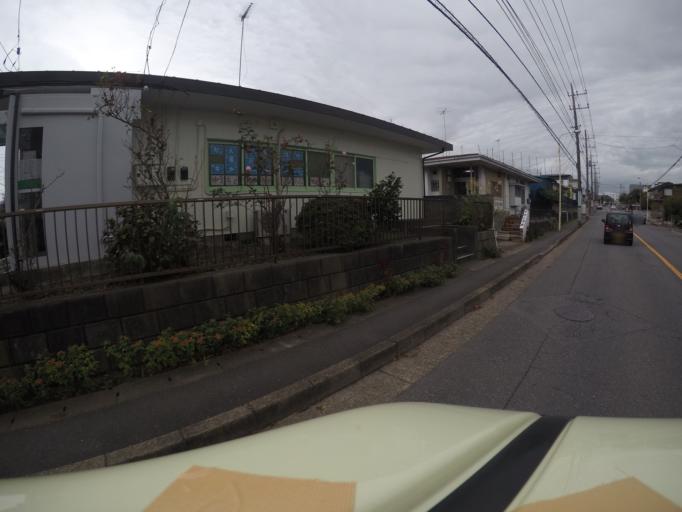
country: JP
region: Ibaraki
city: Naka
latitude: 36.0678
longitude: 140.1732
